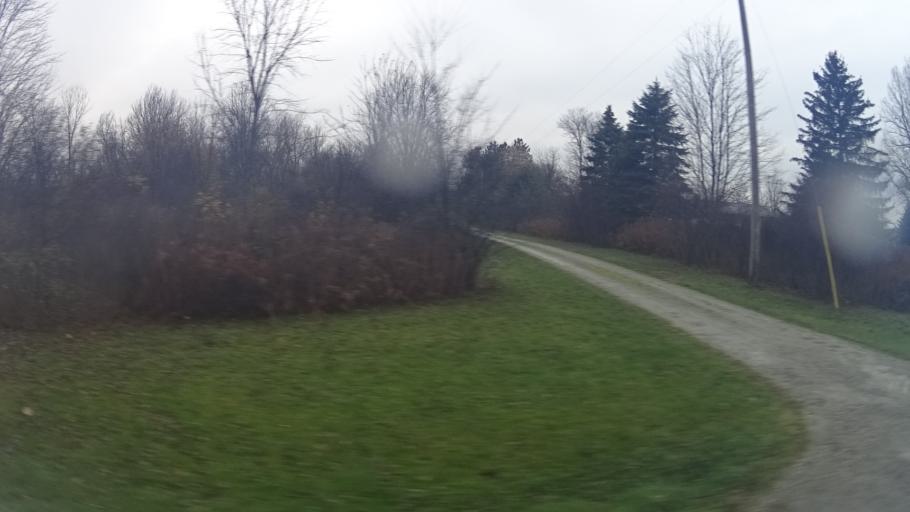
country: US
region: Ohio
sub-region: Lorain County
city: Lagrange
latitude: 41.2569
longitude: -82.1576
